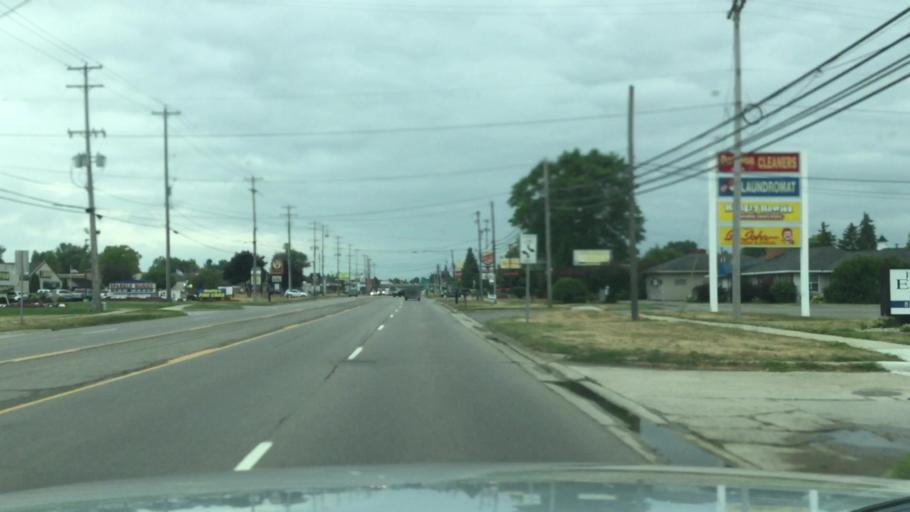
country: US
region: Michigan
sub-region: Genesee County
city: Davison
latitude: 43.0195
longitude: -83.5178
